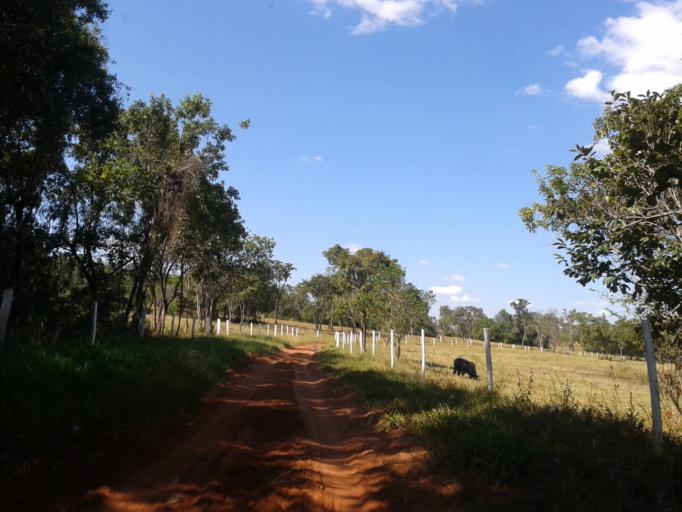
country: BR
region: Minas Gerais
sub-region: Campina Verde
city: Campina Verde
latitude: -19.3850
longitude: -49.7436
